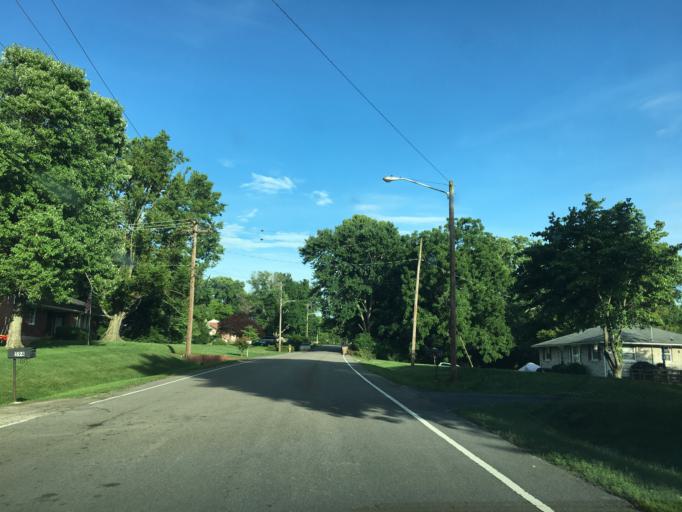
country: US
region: Tennessee
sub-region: Davidson County
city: Oak Hill
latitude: 36.0645
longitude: -86.7327
